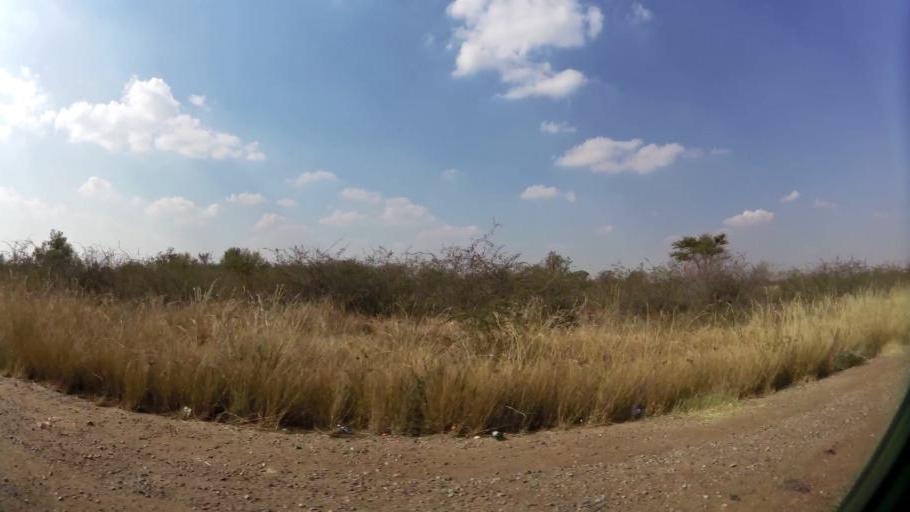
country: ZA
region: North-West
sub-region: Bojanala Platinum District Municipality
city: Rustenburg
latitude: -25.5112
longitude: 27.1000
